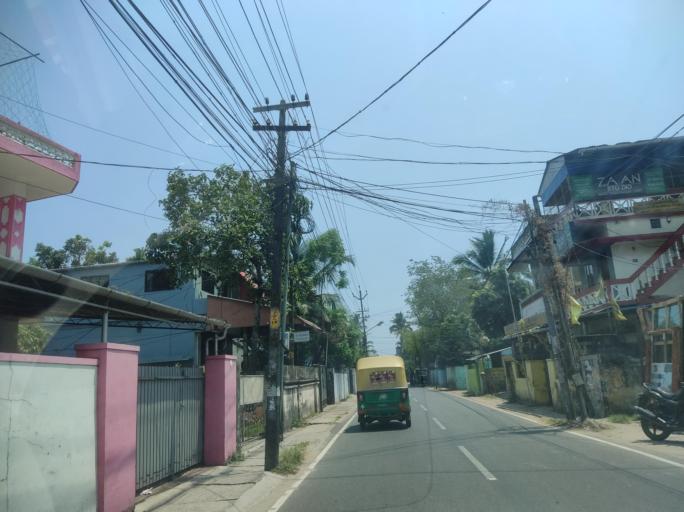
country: IN
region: Kerala
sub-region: Ernakulam
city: Cochin
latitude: 9.9123
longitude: 76.2793
